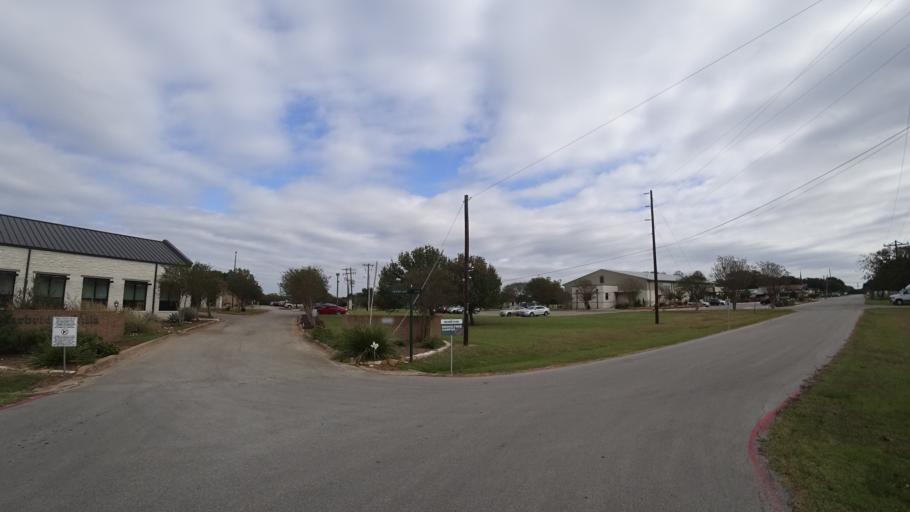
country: US
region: Texas
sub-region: Travis County
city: Manchaca
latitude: 30.1375
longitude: -97.8568
